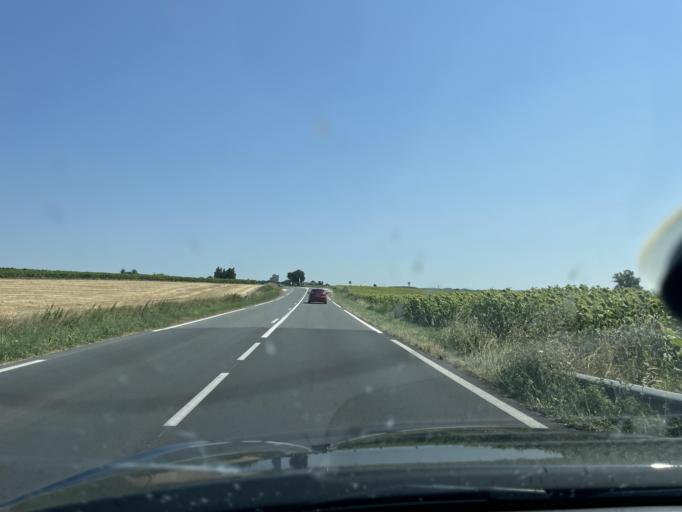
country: FR
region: Poitou-Charentes
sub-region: Departement de la Charente-Maritime
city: Mortagne-sur-Gironde
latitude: 45.4660
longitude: -0.7039
